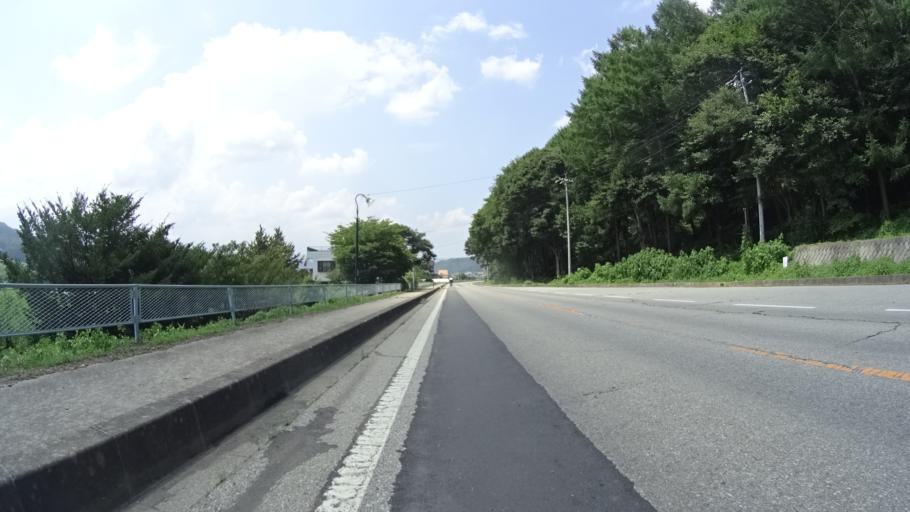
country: JP
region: Nagano
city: Saku
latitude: 36.1475
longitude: 138.5144
